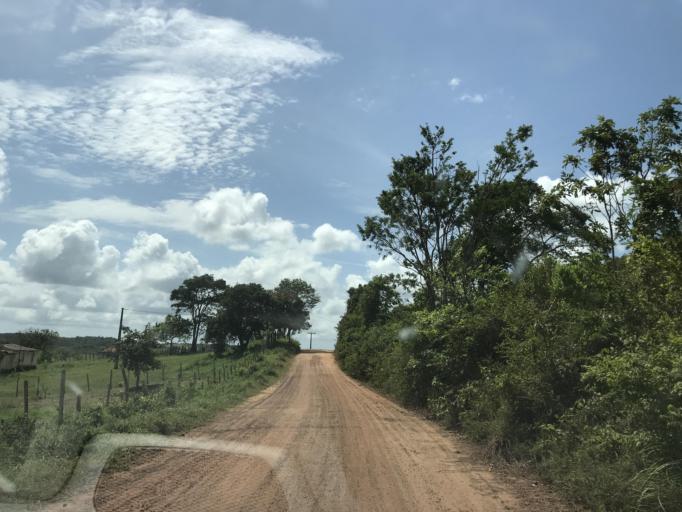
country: BR
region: Bahia
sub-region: Entre Rios
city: Entre Rios
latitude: -12.1816
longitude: -38.0586
